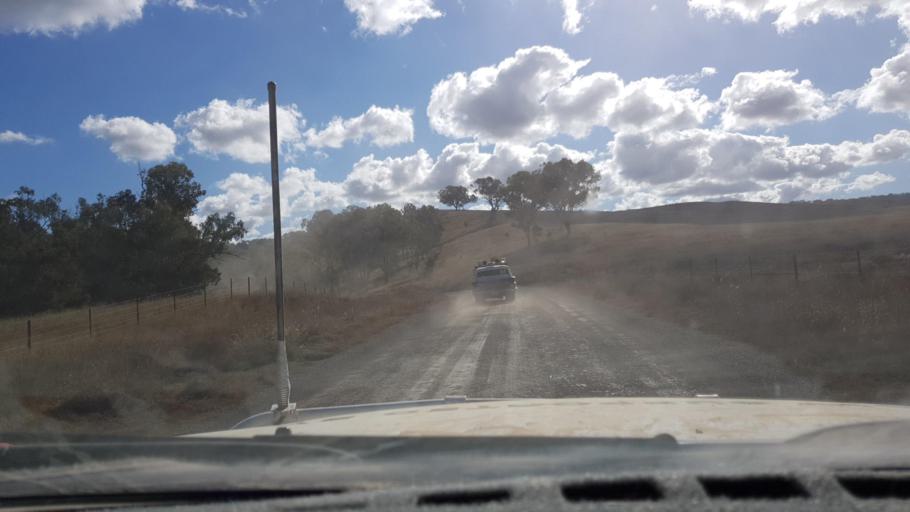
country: AU
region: New South Wales
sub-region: Tamworth Municipality
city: Manilla
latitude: -30.6147
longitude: 150.5146
